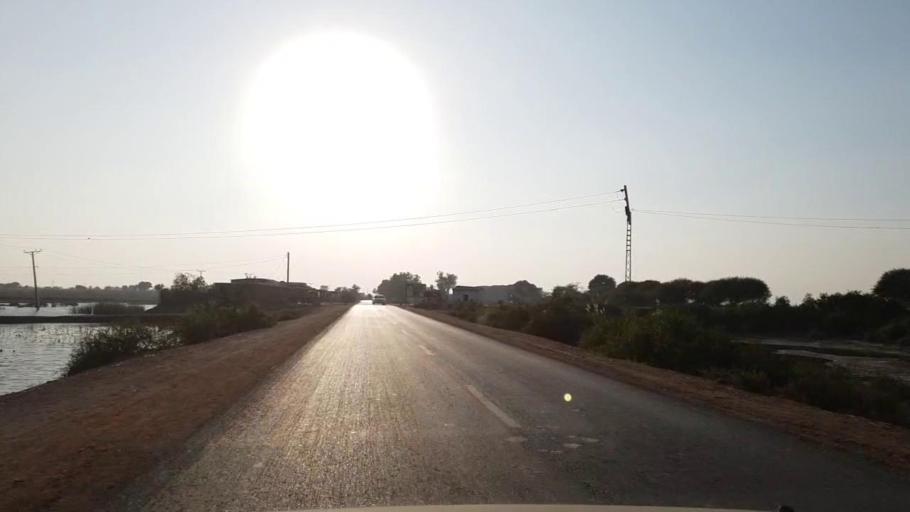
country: PK
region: Sindh
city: Mirpur Batoro
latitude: 24.6849
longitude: 68.1640
